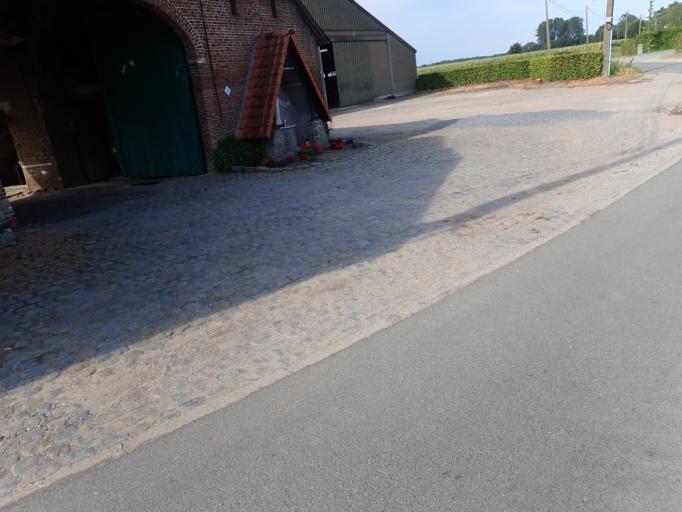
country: BE
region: Flanders
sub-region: Provincie Antwerpen
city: Sint-Amands
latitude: 51.0657
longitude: 4.2314
